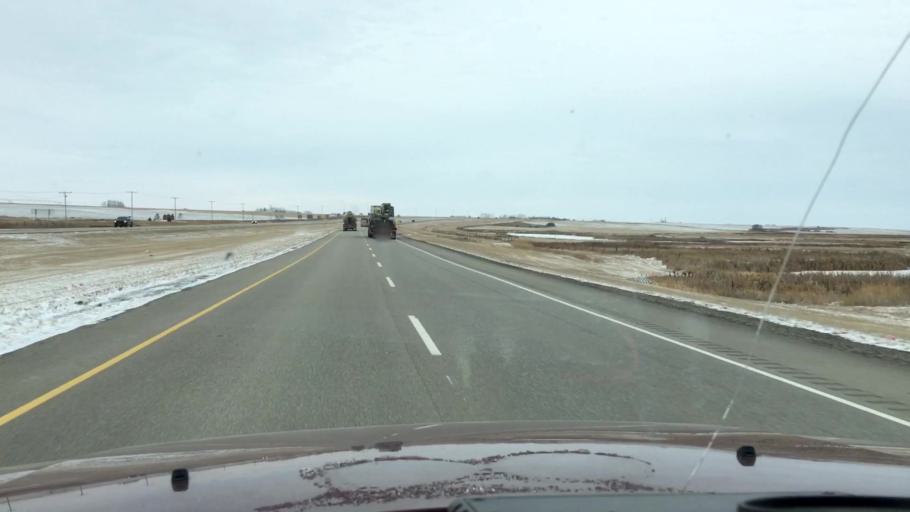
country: CA
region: Saskatchewan
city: Watrous
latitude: 51.2402
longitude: -105.9651
